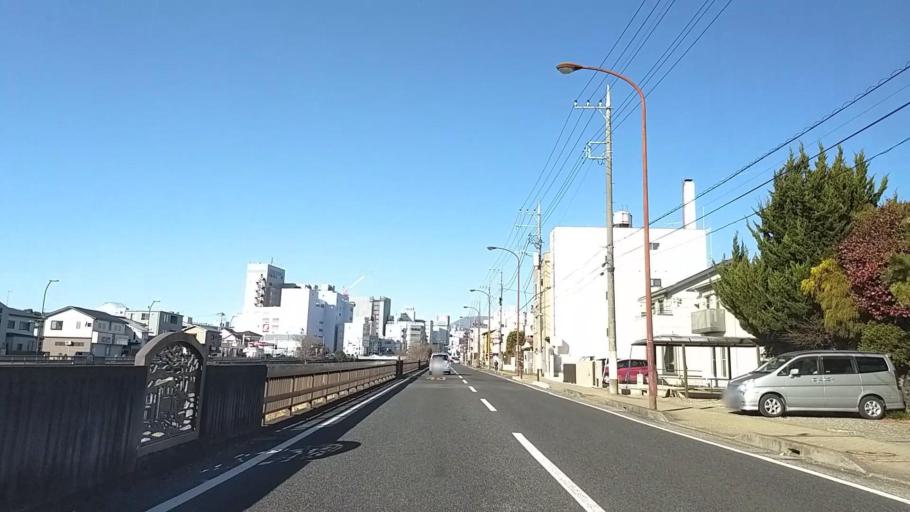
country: JP
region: Kanagawa
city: Hadano
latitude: 35.3695
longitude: 139.2310
